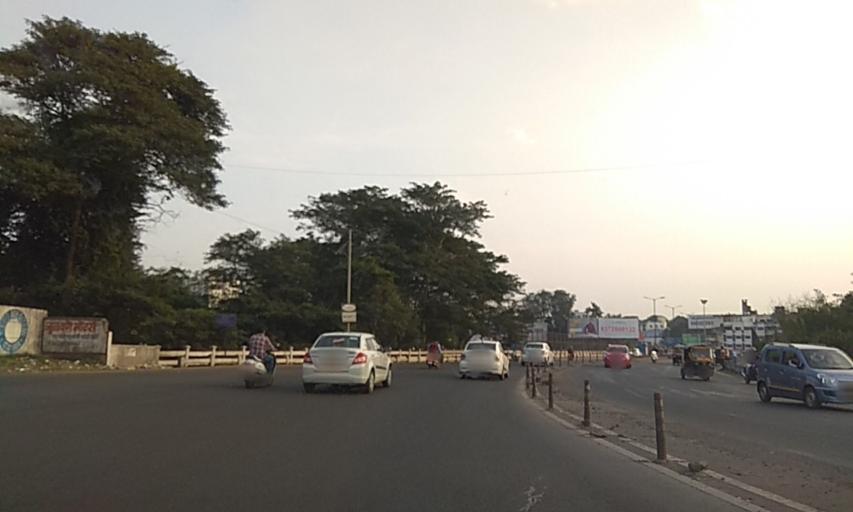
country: IN
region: Maharashtra
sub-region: Pune Division
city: Khadki
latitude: 18.5690
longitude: 73.8114
